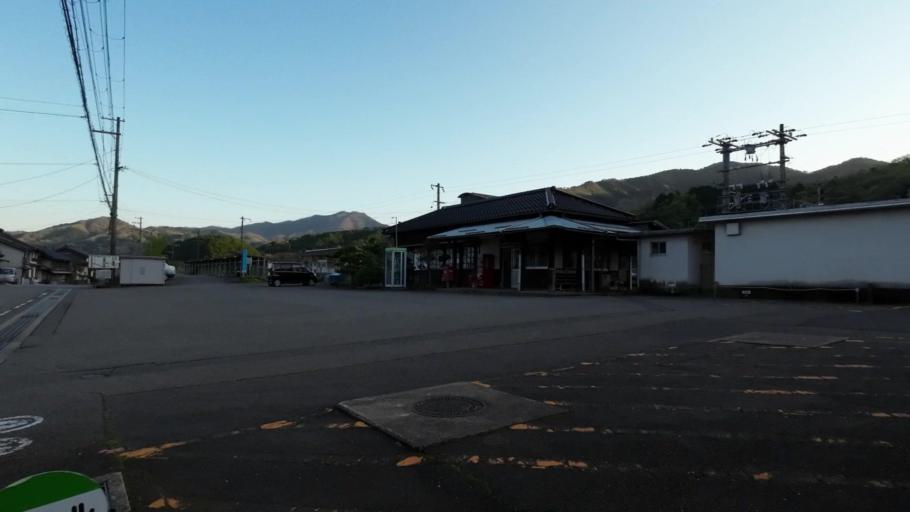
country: JP
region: Hyogo
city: Toyooka
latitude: 35.3716
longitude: 134.8118
